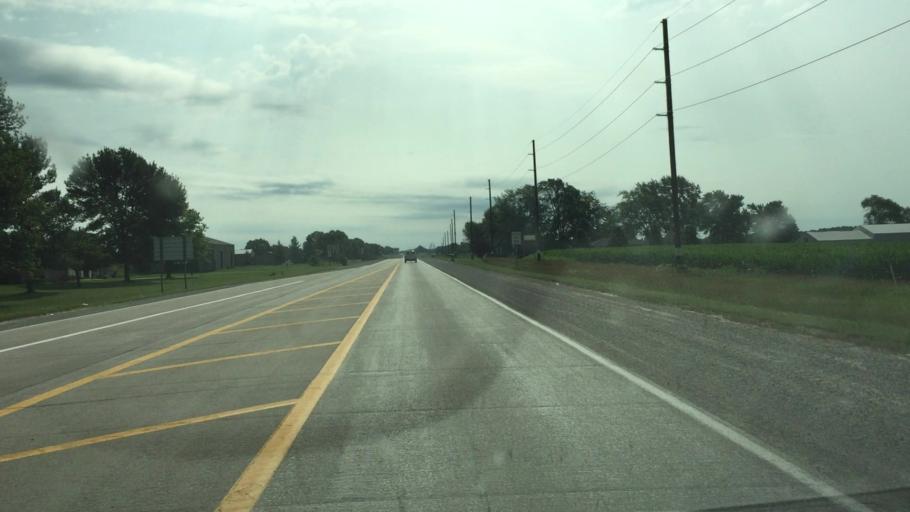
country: US
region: Illinois
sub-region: Hancock County
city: Nauvoo
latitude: 40.6390
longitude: -91.5540
